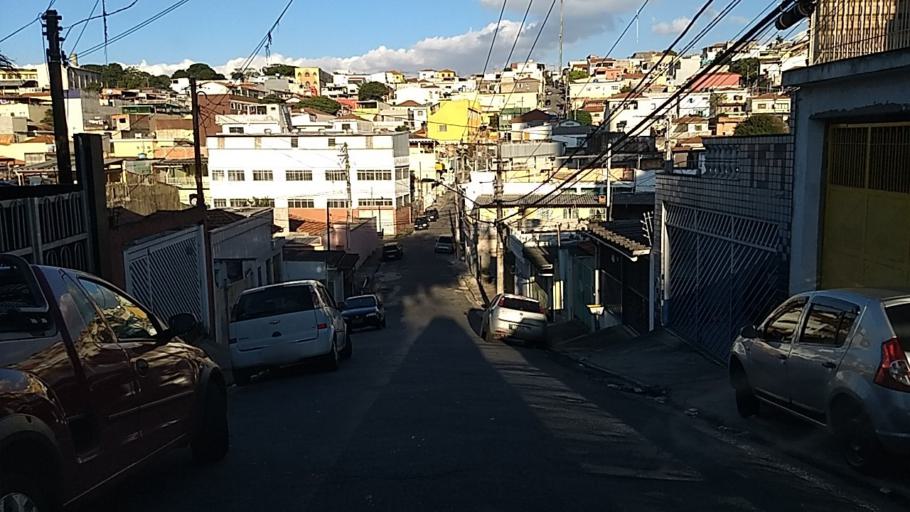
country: BR
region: Sao Paulo
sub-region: Guarulhos
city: Guarulhos
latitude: -23.4921
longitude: -46.5898
